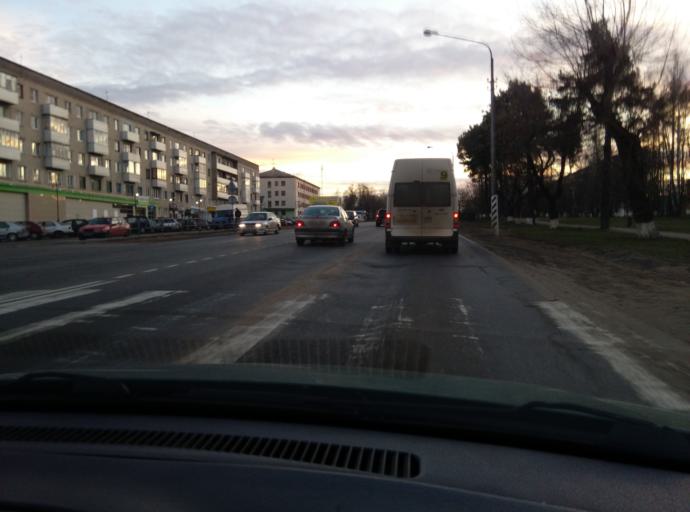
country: BY
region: Minsk
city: Horad Barysaw
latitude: 54.2158
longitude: 28.4894
